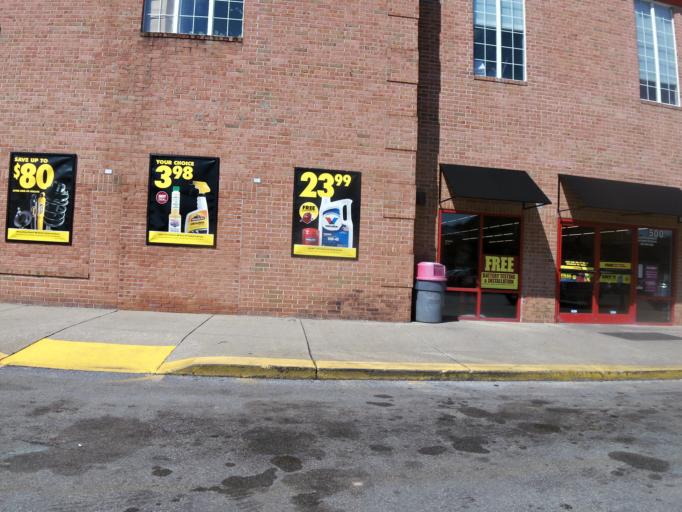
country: US
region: Kentucky
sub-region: Clay County
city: Manchester
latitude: 37.1379
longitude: -83.7706
